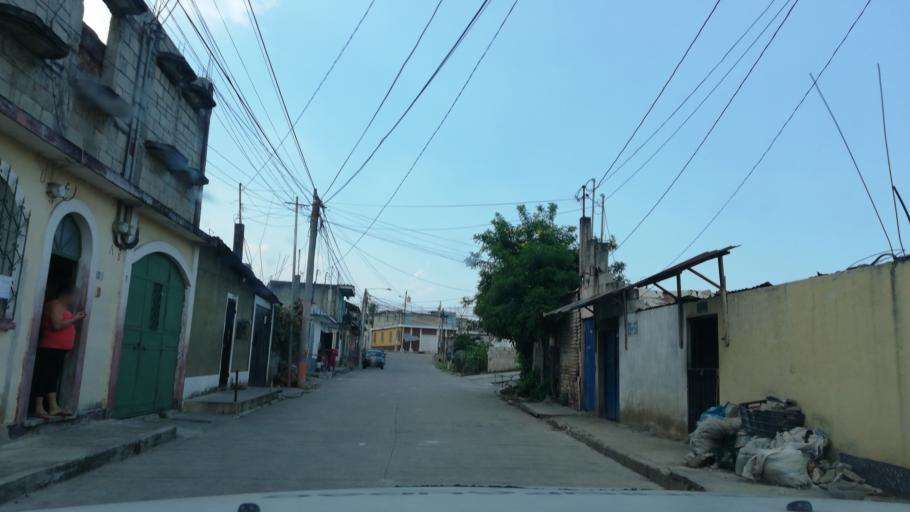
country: GT
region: Guatemala
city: Petapa
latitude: 14.5100
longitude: -90.5663
